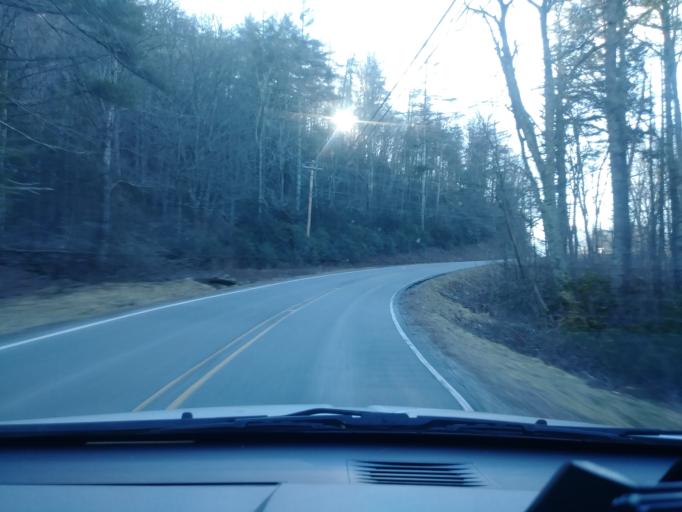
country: US
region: North Carolina
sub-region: Avery County
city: Banner Elk
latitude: 36.1658
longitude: -81.9037
